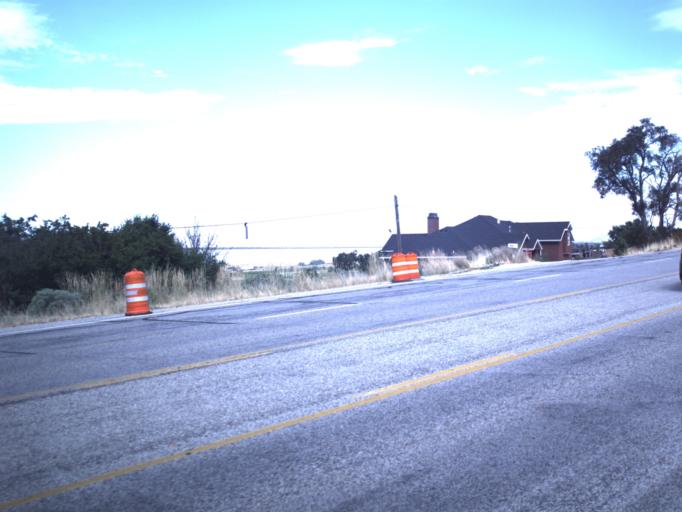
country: US
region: Utah
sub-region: Box Elder County
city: Willard
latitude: 41.3870
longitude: -112.0325
